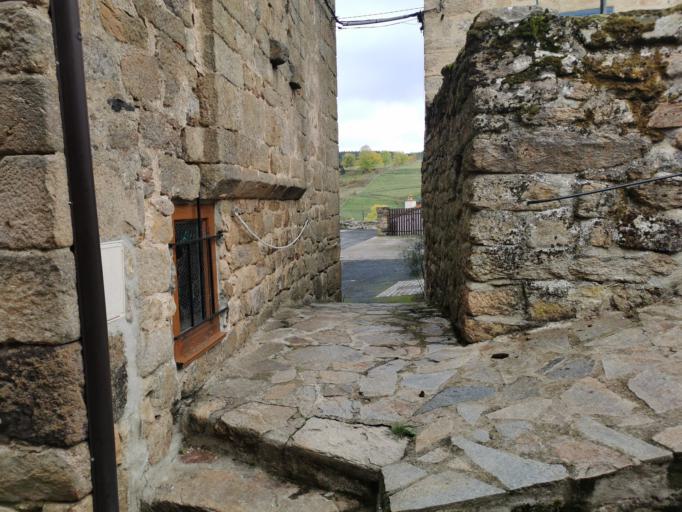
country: FR
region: Languedoc-Roussillon
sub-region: Departement de la Lozere
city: Langogne
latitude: 44.7685
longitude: 3.8832
